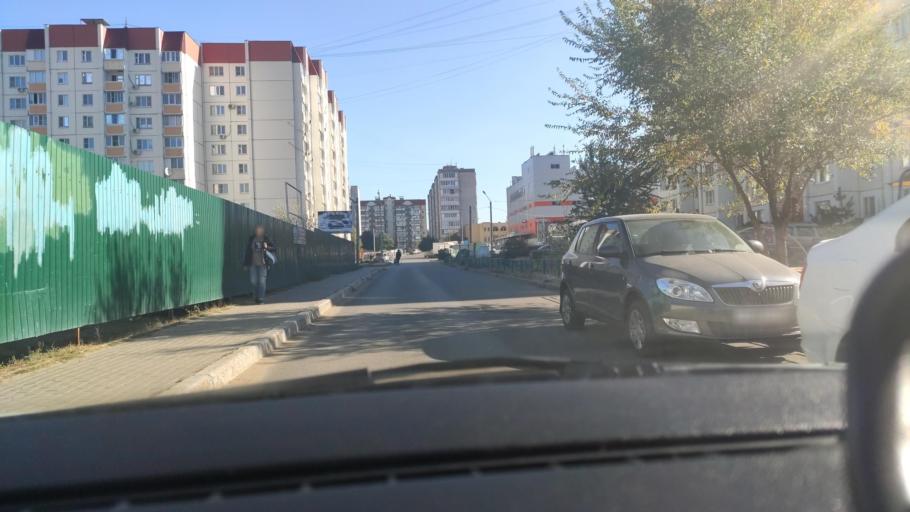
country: RU
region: Voronezj
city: Pridonskoy
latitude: 51.6254
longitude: 39.0752
